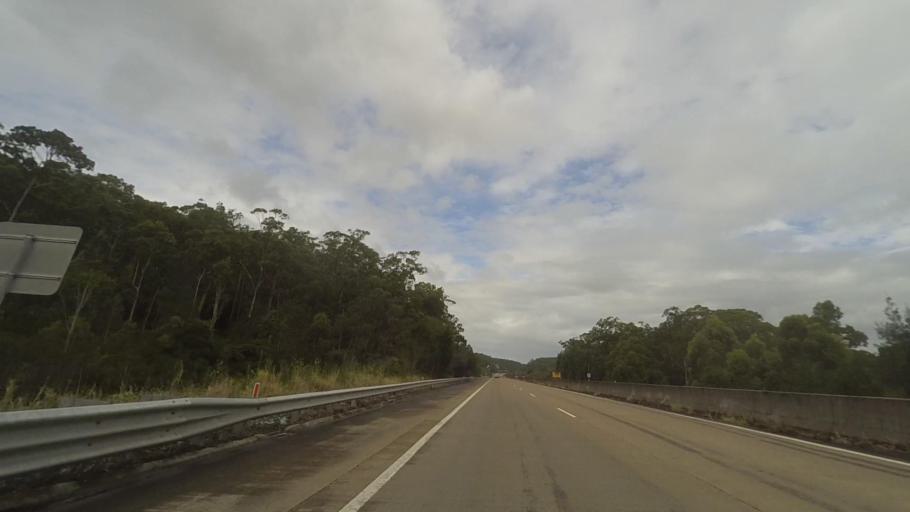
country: AU
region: New South Wales
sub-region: Port Stephens Shire
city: Port Stephens
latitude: -32.6226
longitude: 151.9536
